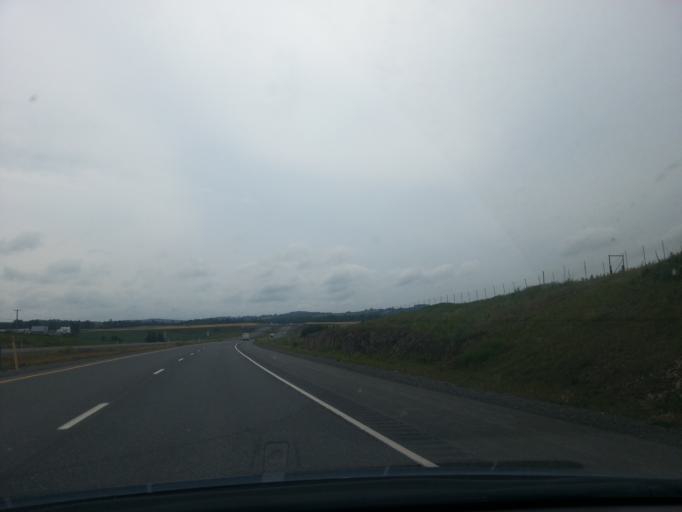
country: CA
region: New Brunswick
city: Florenceville-Bristol
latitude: 46.2788
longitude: -67.5825
